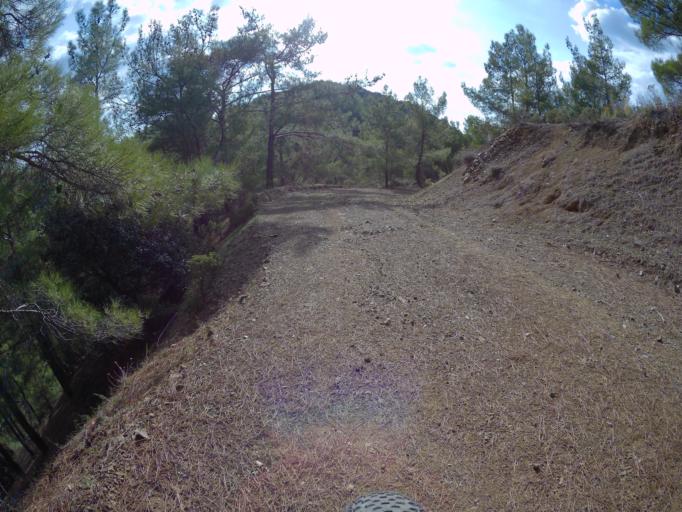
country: CY
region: Limassol
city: Pachna
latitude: 34.9127
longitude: 32.7867
